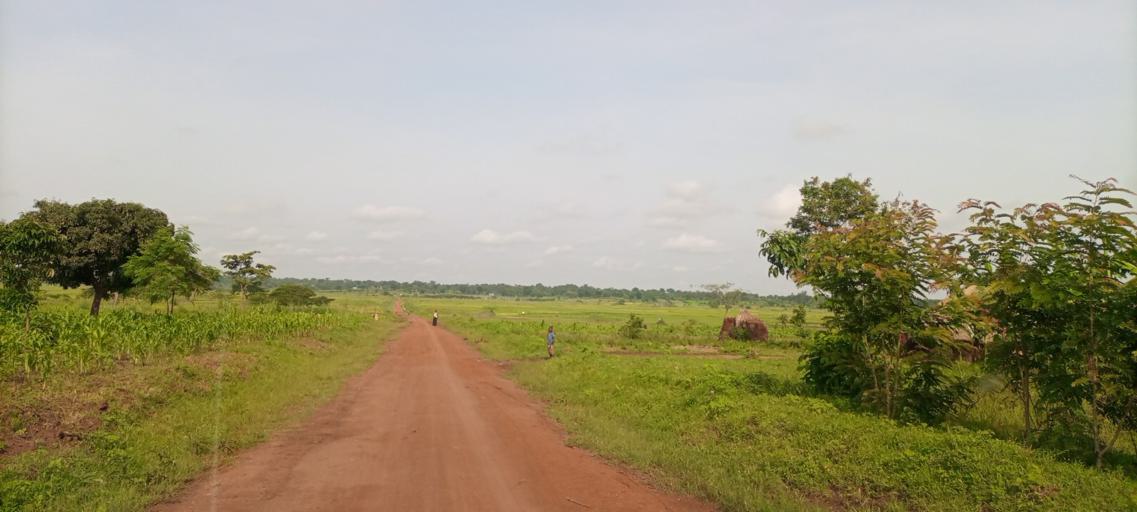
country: UG
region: Eastern Region
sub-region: Kibuku District
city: Kibuku
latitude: 1.1025
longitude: 33.7790
